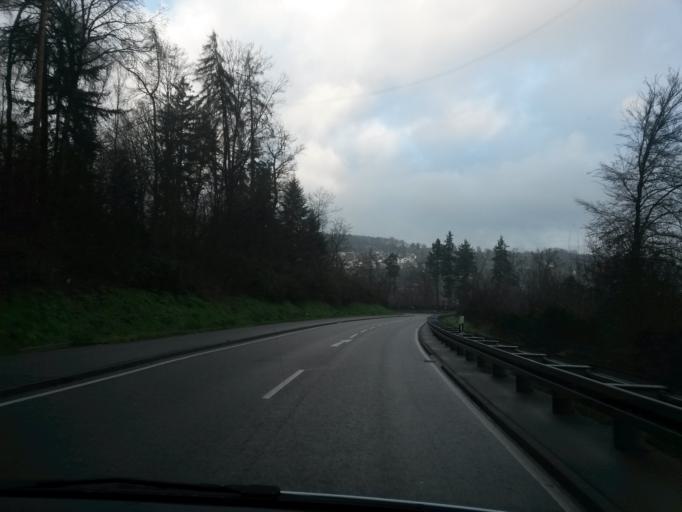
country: DE
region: Baden-Wuerttemberg
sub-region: Karlsruhe Region
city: Eutingen
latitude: 48.8944
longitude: 8.7335
